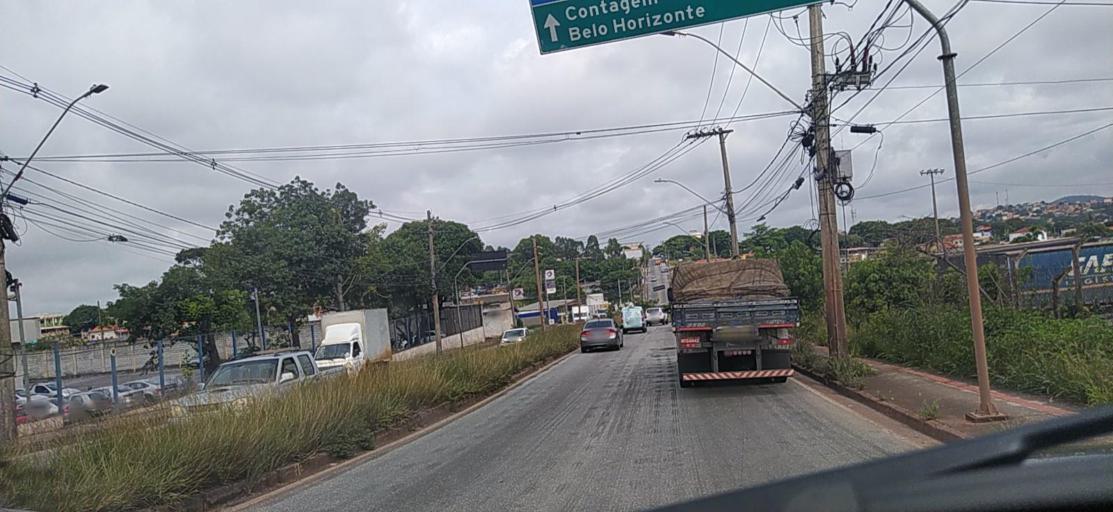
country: BR
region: Minas Gerais
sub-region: Betim
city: Betim
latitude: -19.9539
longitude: -44.1509
